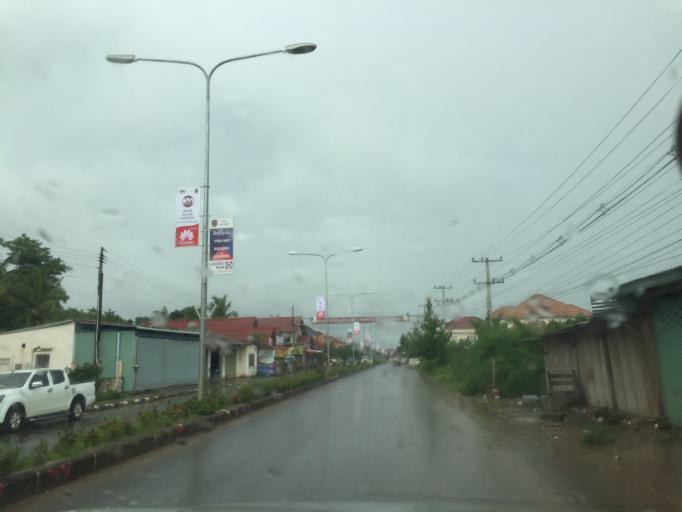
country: LA
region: Attapu
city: Attapu
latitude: 14.8198
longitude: 106.8135
